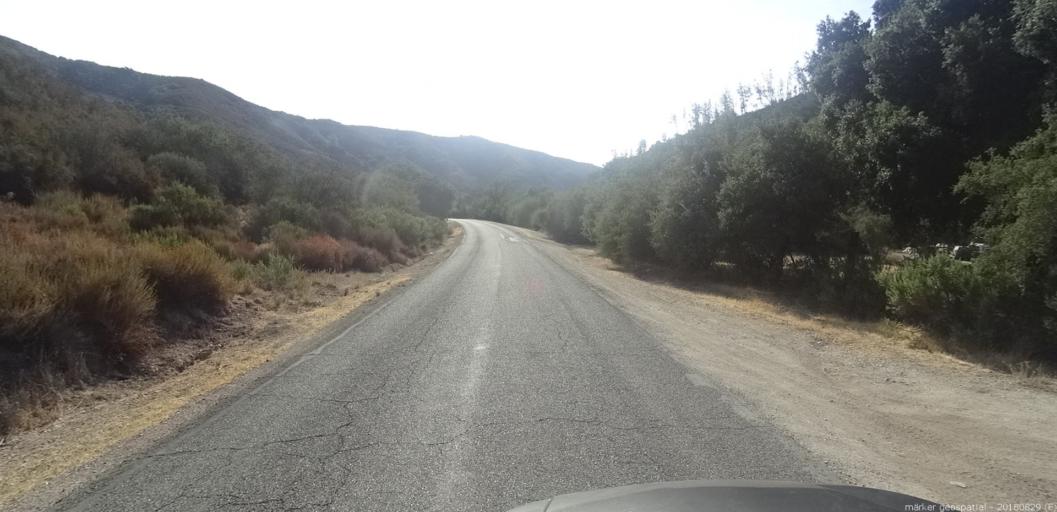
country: US
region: California
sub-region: Monterey County
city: King City
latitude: 36.0285
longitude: -121.0738
